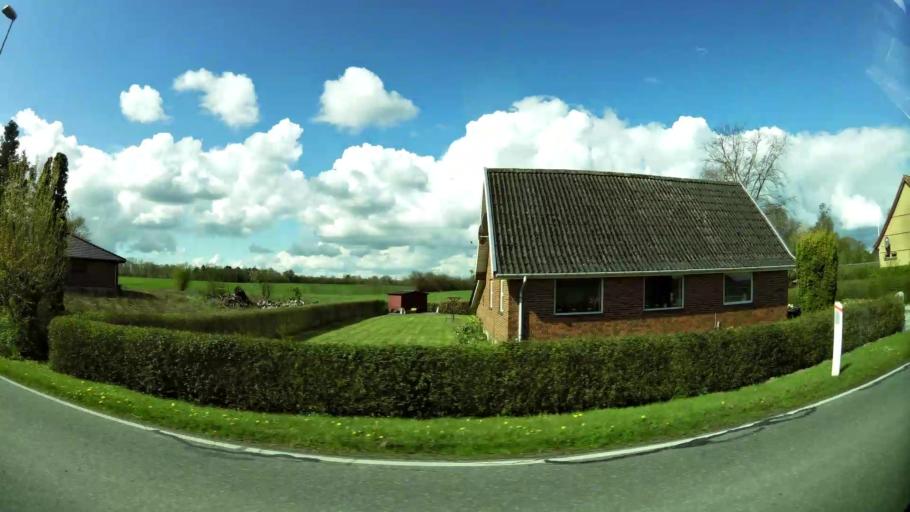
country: DK
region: South Denmark
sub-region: Middelfart Kommune
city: Brenderup
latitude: 55.4664
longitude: 10.0104
